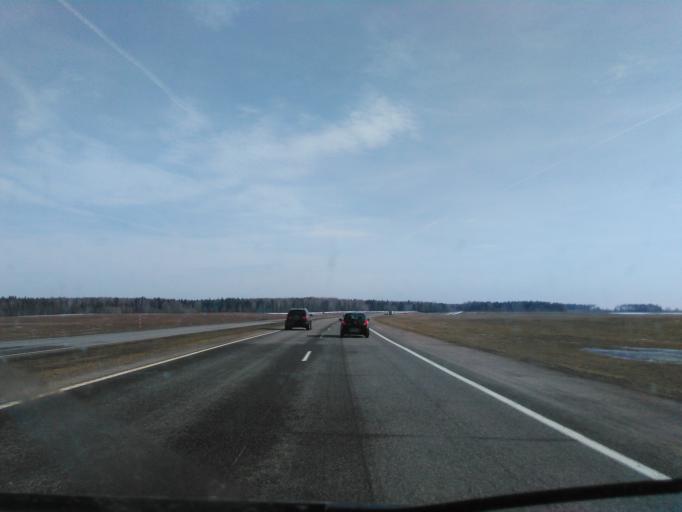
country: BY
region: Vitebsk
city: Talachyn
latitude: 54.4790
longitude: 29.8240
